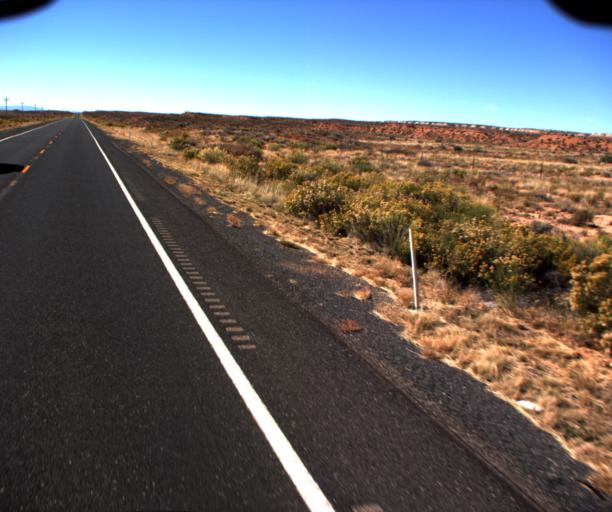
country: US
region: Arizona
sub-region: Coconino County
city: Fredonia
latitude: 36.9189
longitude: -112.5760
